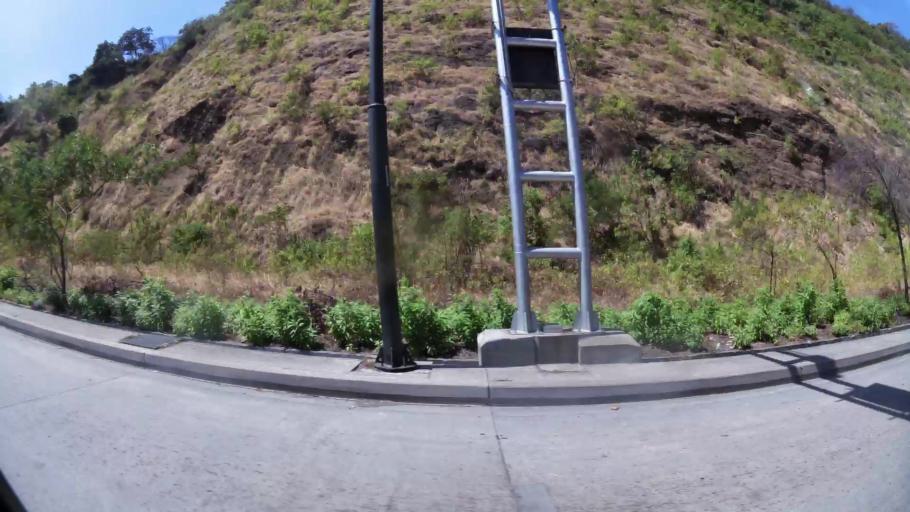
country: EC
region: Guayas
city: Guayaquil
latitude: -2.1781
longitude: -79.9267
